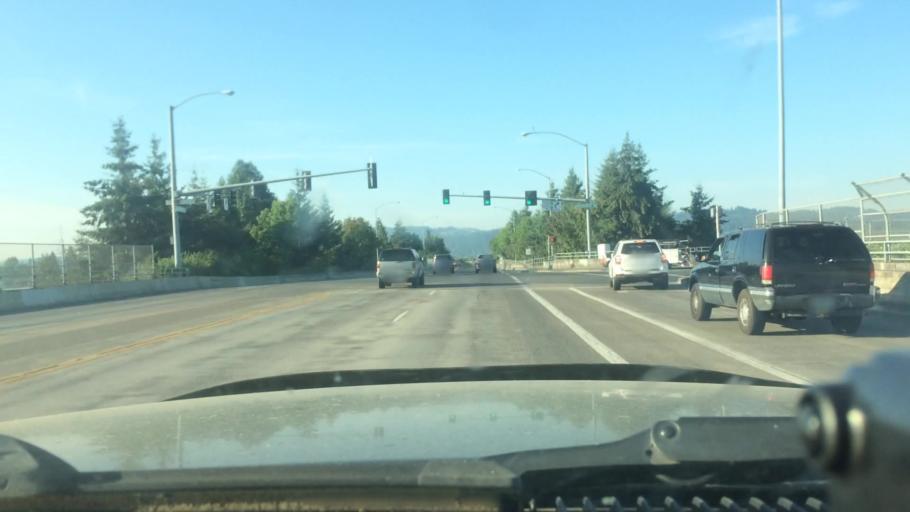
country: US
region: Oregon
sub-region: Lane County
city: Eugene
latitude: 44.0625
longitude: -123.1175
